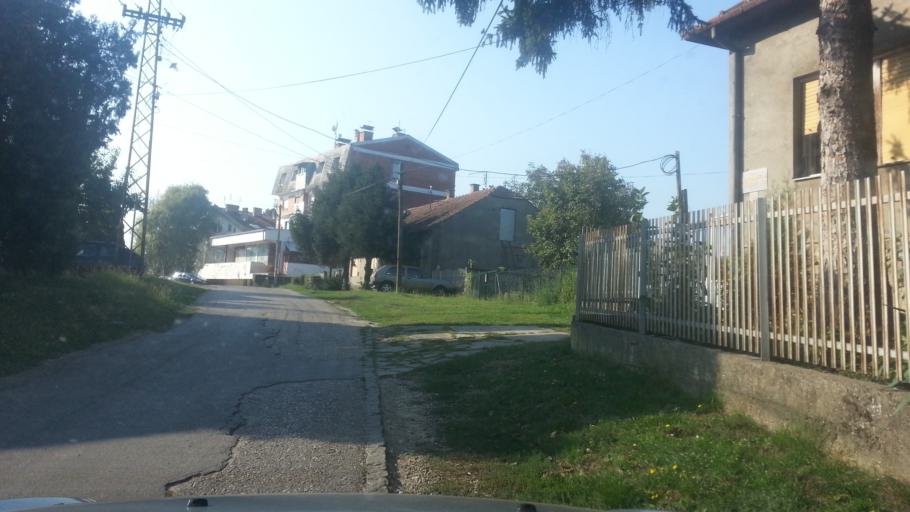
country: RS
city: Novi Banovci
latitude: 44.9514
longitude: 20.2876
